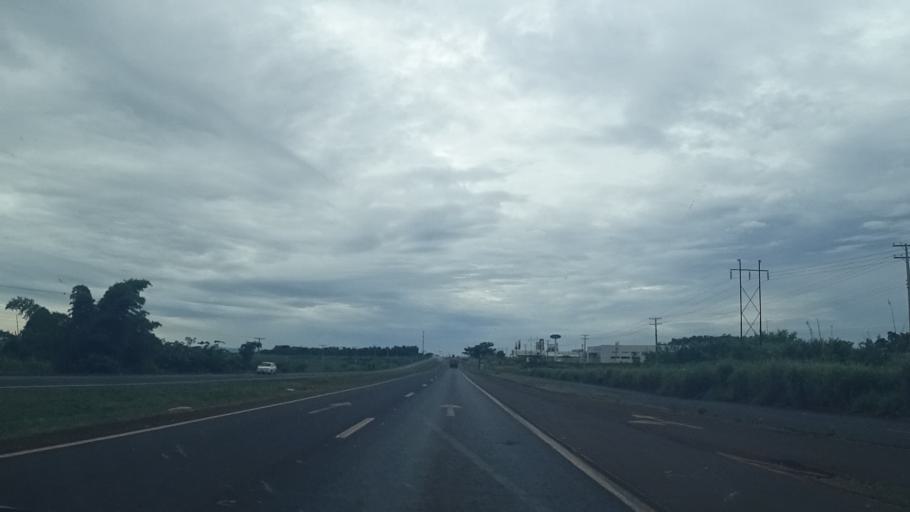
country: BR
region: Goias
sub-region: Itumbiara
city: Itumbiara
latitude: -18.3409
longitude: -49.2225
